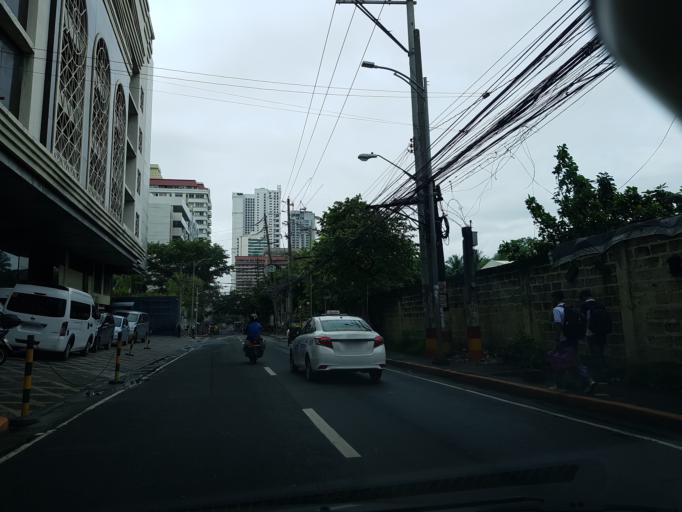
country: PH
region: Metro Manila
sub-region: City of Manila
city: Port Area
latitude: 14.5717
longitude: 120.9831
